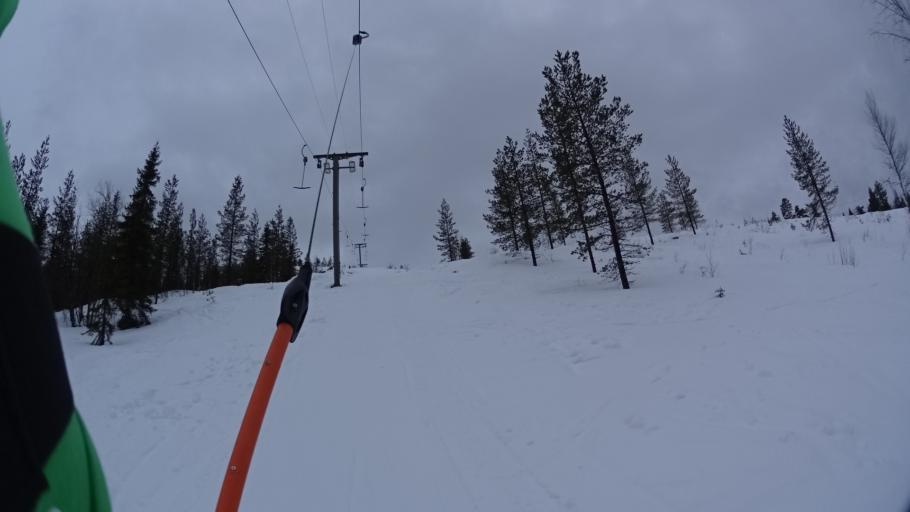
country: SE
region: Vaesterbotten
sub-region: Mala Kommun
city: Mala
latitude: 65.1795
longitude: 18.7685
